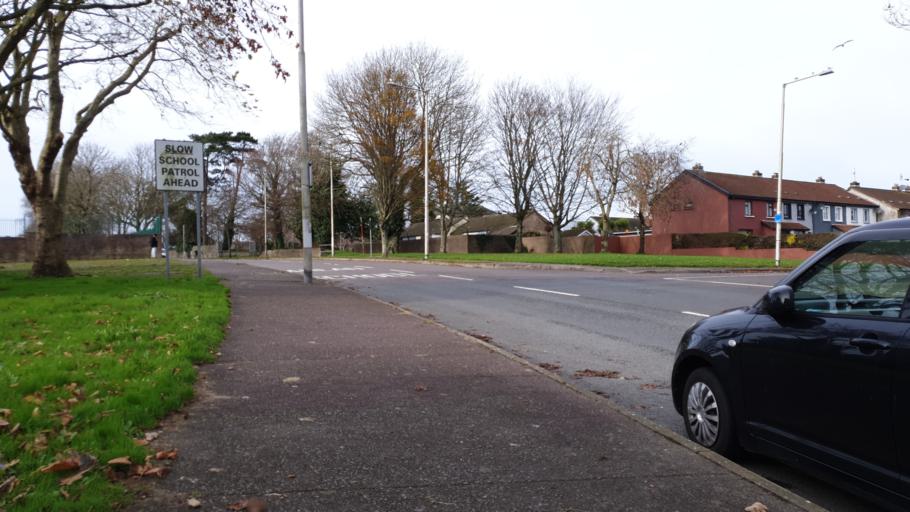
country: IE
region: Munster
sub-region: County Cork
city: Passage West
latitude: 51.8949
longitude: -8.4002
